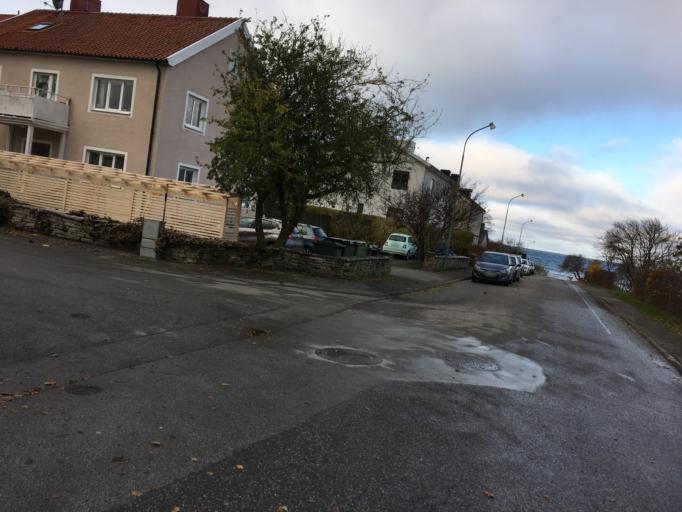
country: SE
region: Gotland
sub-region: Gotland
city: Visby
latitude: 57.6515
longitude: 18.3049
